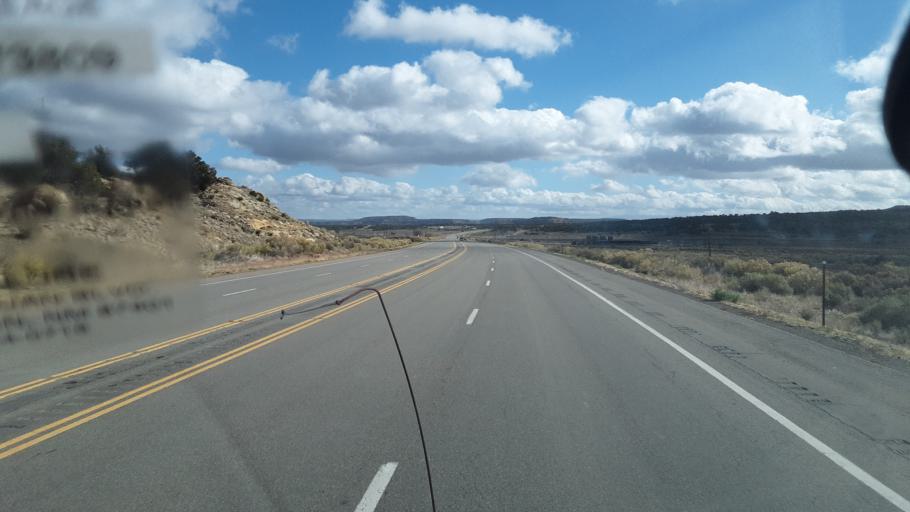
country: US
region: New Mexico
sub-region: San Juan County
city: Bloomfield
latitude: 36.2258
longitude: -107.5260
